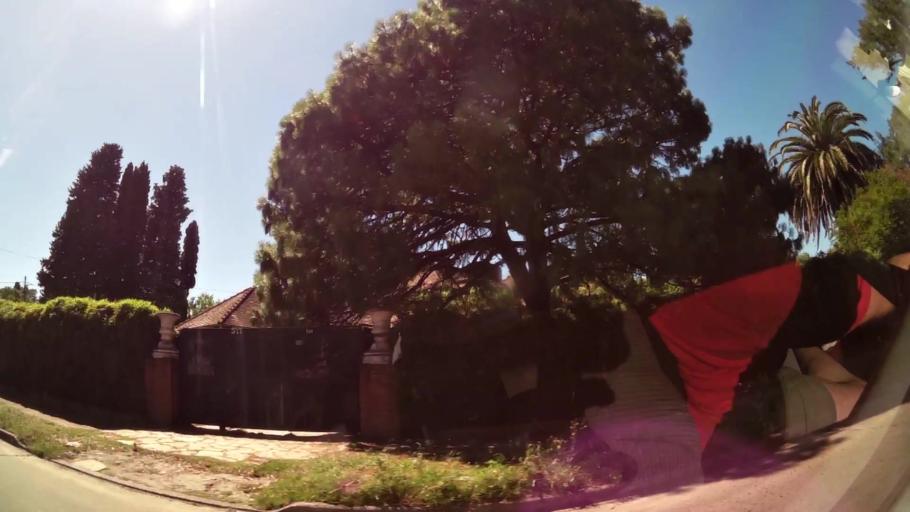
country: AR
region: Buenos Aires
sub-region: Partido de Tigre
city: Tigre
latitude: -34.4997
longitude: -58.6171
